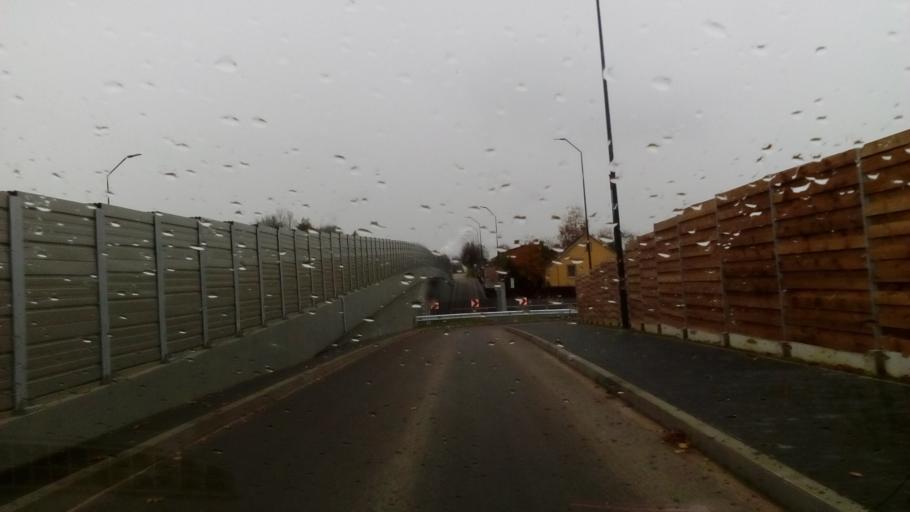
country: LT
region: Marijampoles apskritis
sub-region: Marijampole Municipality
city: Marijampole
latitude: 54.5452
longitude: 23.3560
